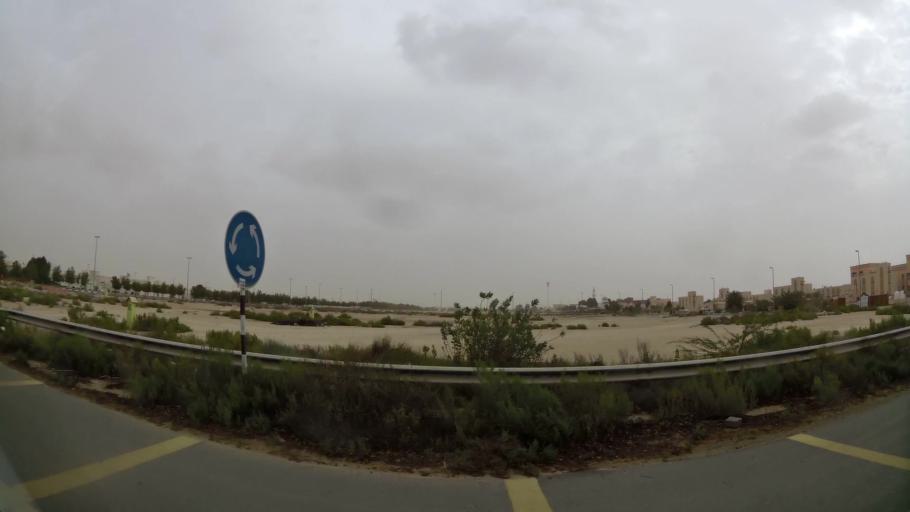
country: AE
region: Abu Dhabi
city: Abu Dhabi
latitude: 24.3845
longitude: 54.6958
